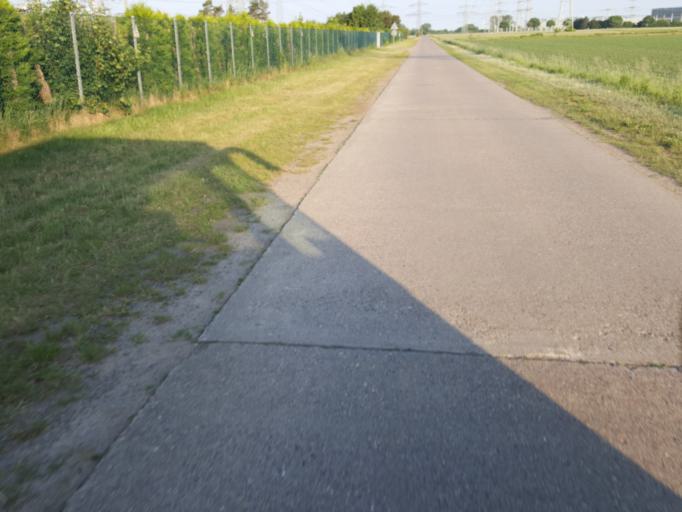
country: DE
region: Lower Saxony
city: Landesbergen
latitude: 52.5402
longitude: 9.1276
